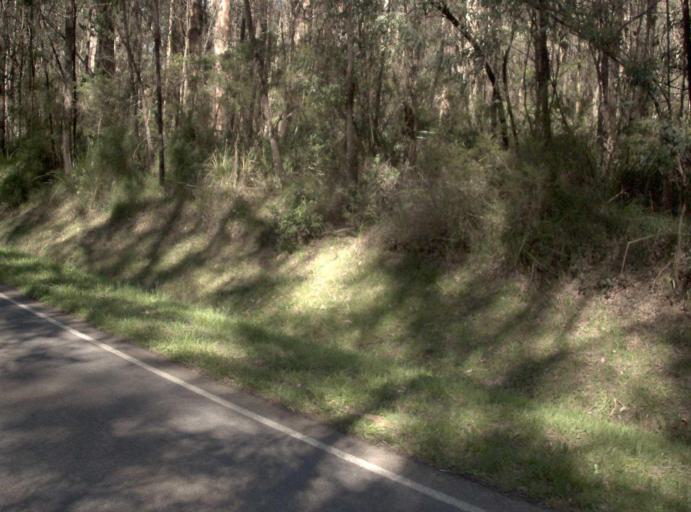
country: AU
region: Victoria
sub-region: Yarra Ranges
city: Millgrove
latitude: -37.8821
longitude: 145.8606
